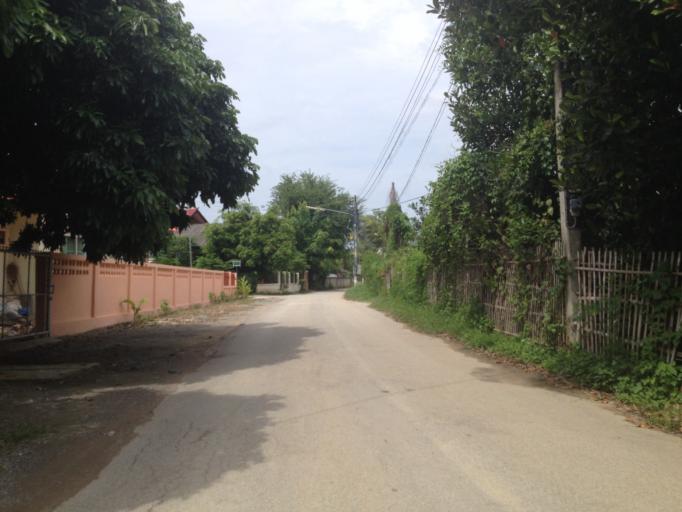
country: TH
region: Chiang Mai
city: Hang Dong
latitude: 18.7042
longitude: 98.9427
